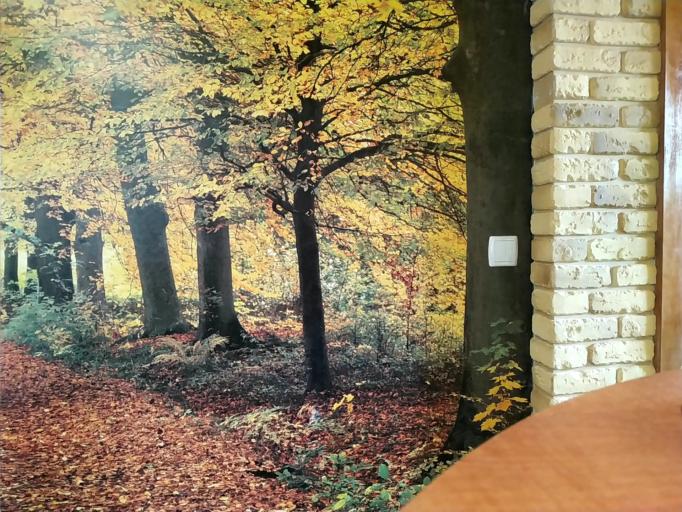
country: RU
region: Novgorod
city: Opechenskiy Posad
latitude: 58.2730
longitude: 33.9964
